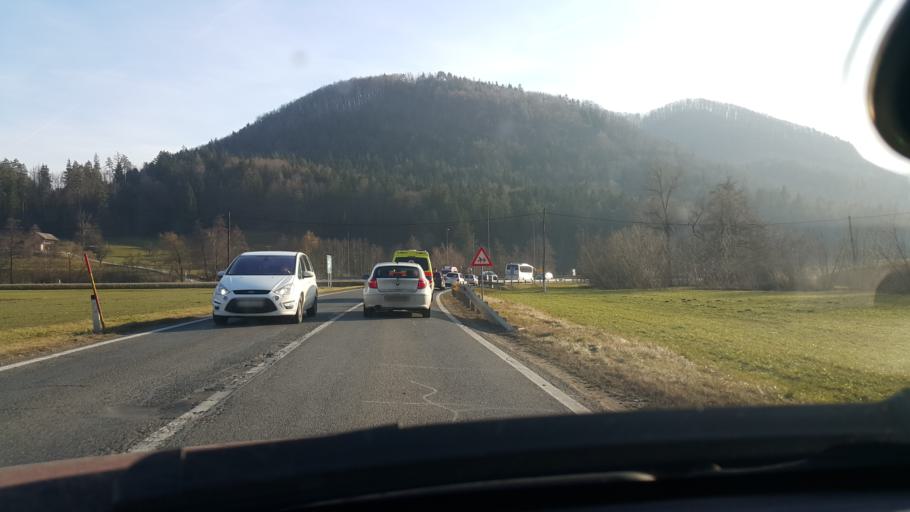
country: SI
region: Dobrna
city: Dobrna
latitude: 46.3247
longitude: 15.1839
